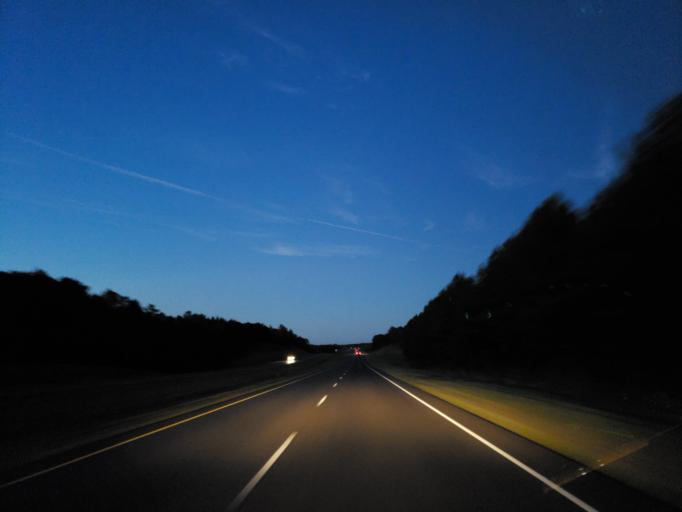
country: US
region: Mississippi
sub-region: Clarke County
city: Quitman
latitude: 32.0243
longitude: -88.6838
